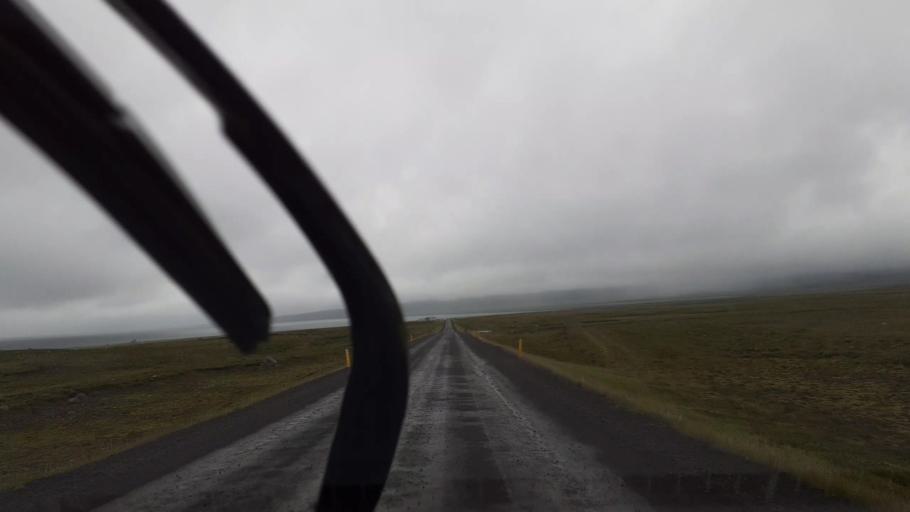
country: IS
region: East
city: Egilsstadir
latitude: 66.0756
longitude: -15.1054
